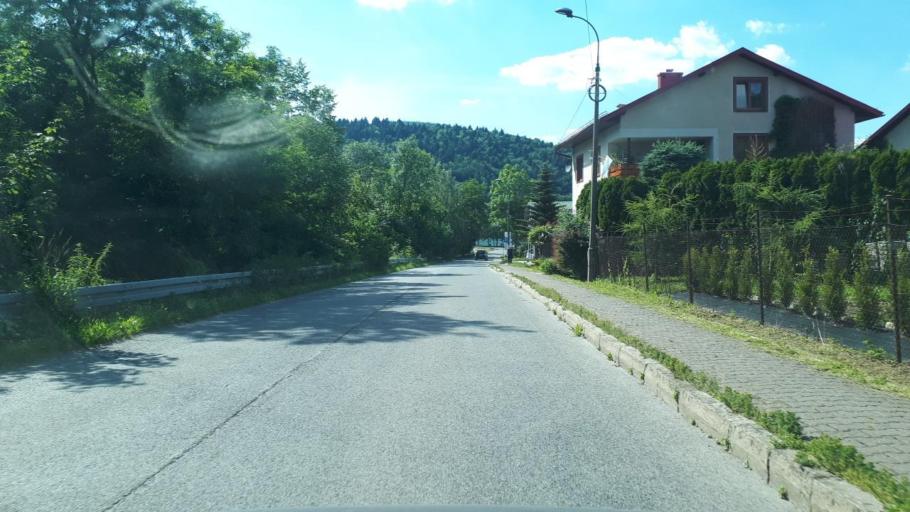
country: PL
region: Silesian Voivodeship
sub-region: Powiat zywiecki
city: Czernichow
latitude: 49.7663
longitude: 19.2097
